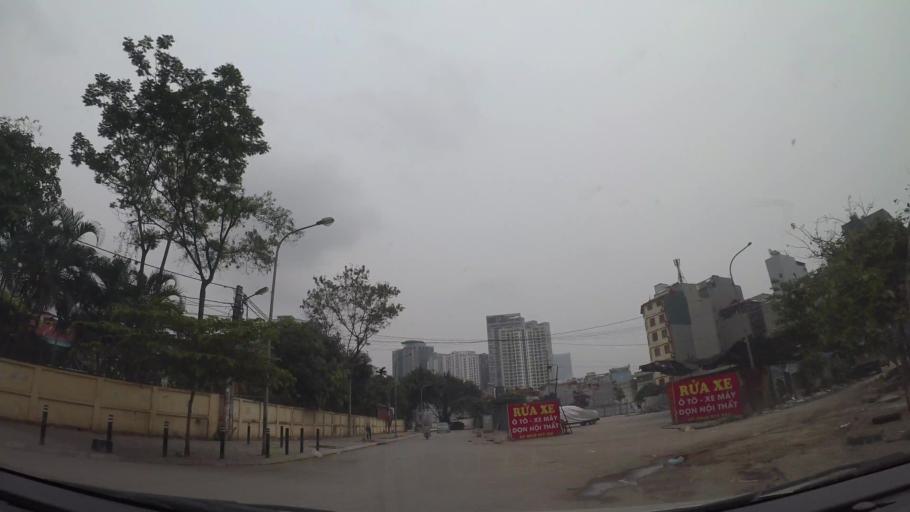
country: VN
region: Ha Noi
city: Cau Dien
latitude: 21.0341
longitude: 105.7733
